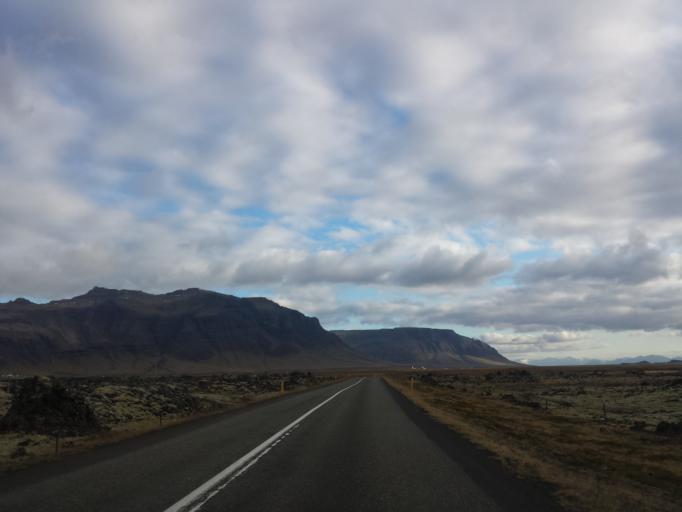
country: IS
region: West
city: Borgarnes
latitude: 64.8358
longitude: -22.2956
